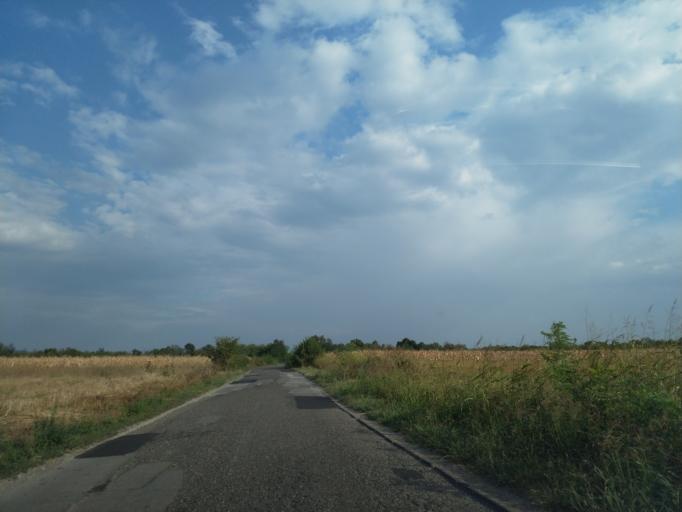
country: RS
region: Central Serbia
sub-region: Pomoravski Okrug
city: Paracin
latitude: 43.8469
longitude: 21.4660
